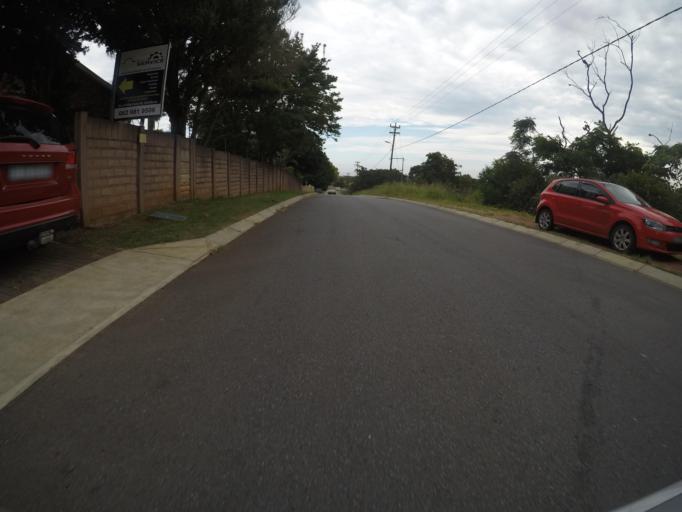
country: ZA
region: Eastern Cape
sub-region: Buffalo City Metropolitan Municipality
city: East London
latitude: -32.9372
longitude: 28.0030
